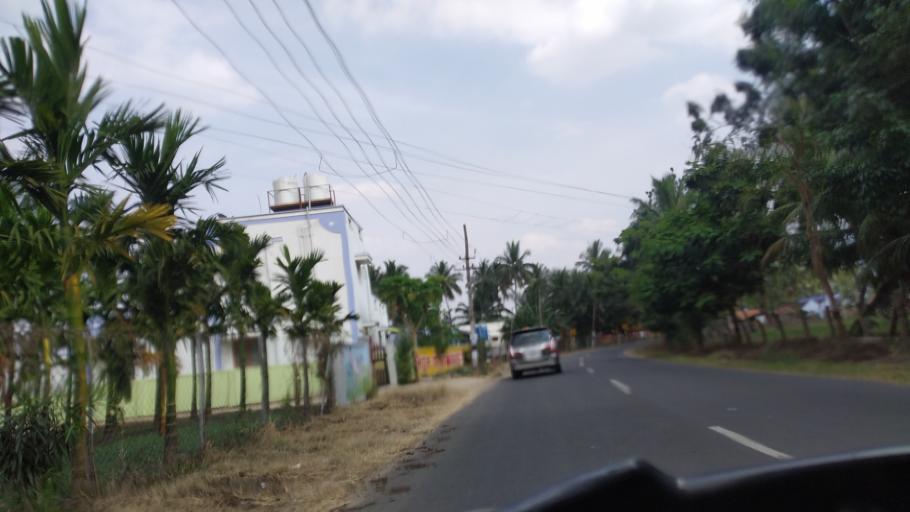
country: IN
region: Tamil Nadu
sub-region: Coimbatore
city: Perur
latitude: 10.9536
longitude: 76.7625
